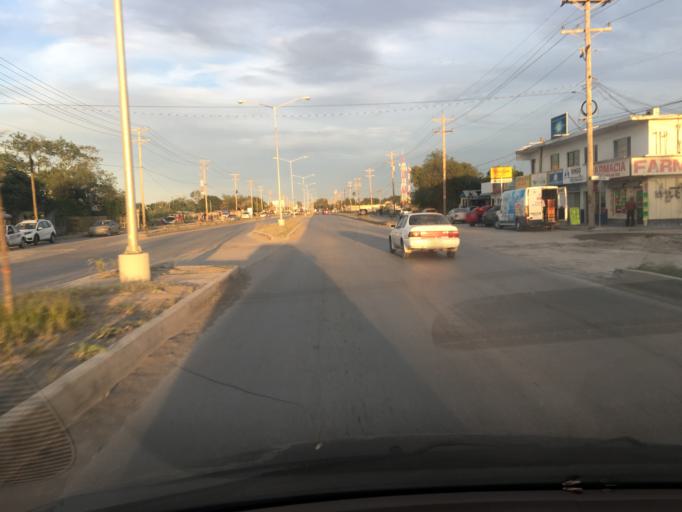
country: MX
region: Tamaulipas
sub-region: Matamoros
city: Heroica Matamoros
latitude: 25.8676
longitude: -97.5615
